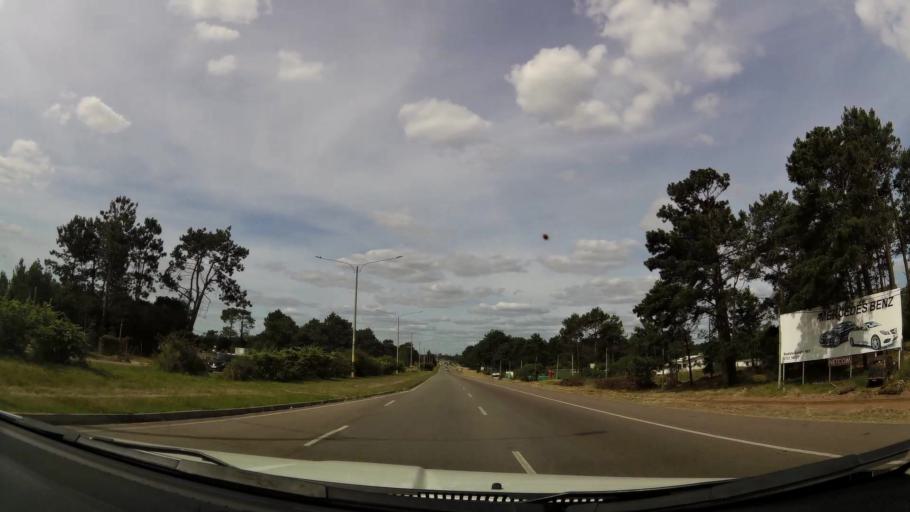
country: UY
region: Canelones
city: Pando
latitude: -34.7931
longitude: -55.9006
